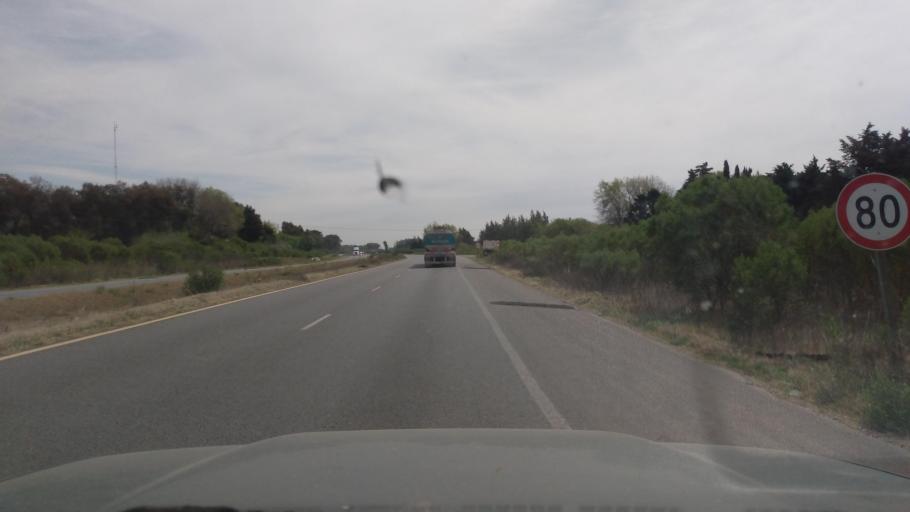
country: AR
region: Buenos Aires
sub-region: Partido de Lujan
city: Lujan
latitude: -34.5053
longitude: -59.0439
